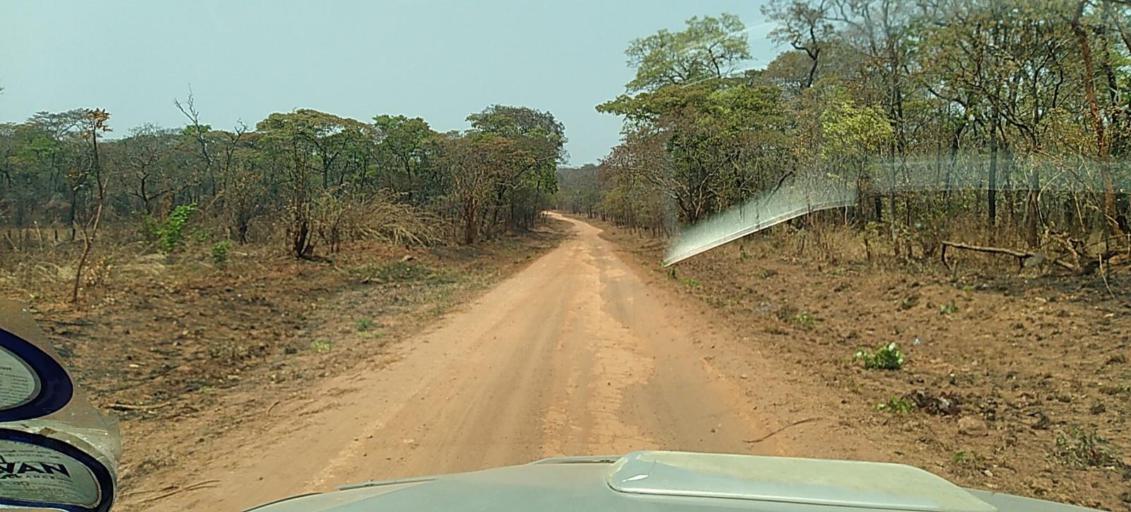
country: ZM
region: North-Western
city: Kasempa
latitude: -13.5503
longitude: 26.0630
